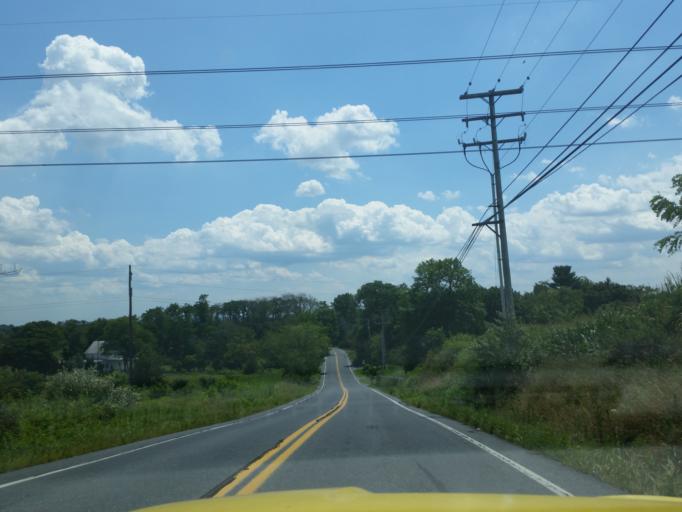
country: US
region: Pennsylvania
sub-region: Lebanon County
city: Palmyra
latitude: 40.4036
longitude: -76.5980
